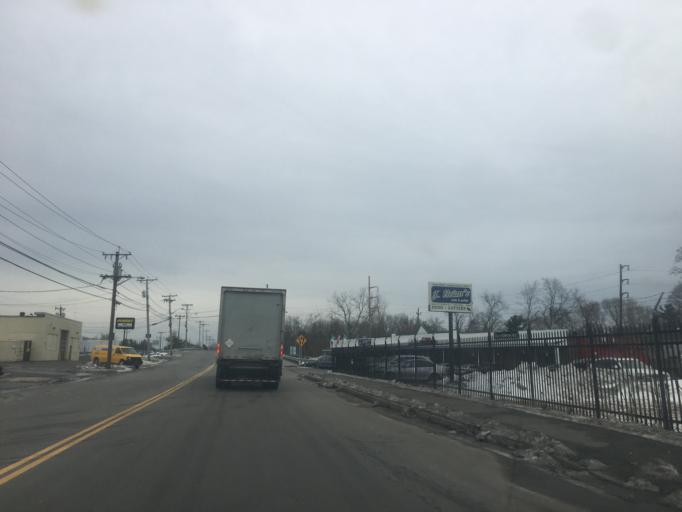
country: US
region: Massachusetts
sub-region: Essex County
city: North Andover
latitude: 42.6862
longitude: -71.1528
